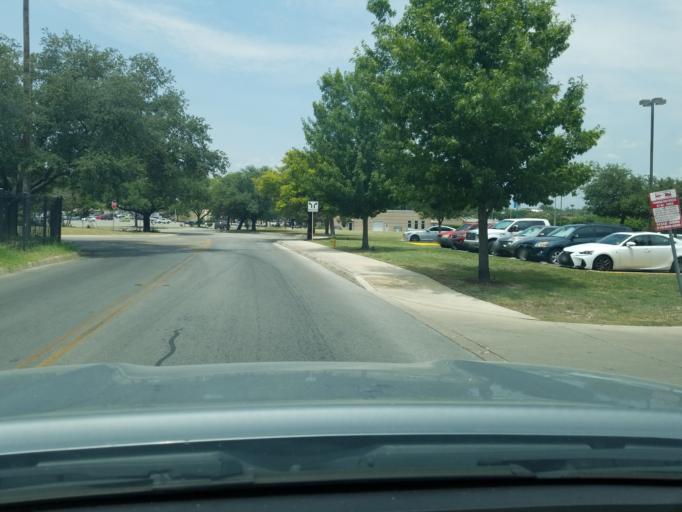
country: US
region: Texas
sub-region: Bexar County
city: Hollywood Park
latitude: 29.5630
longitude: -98.4860
